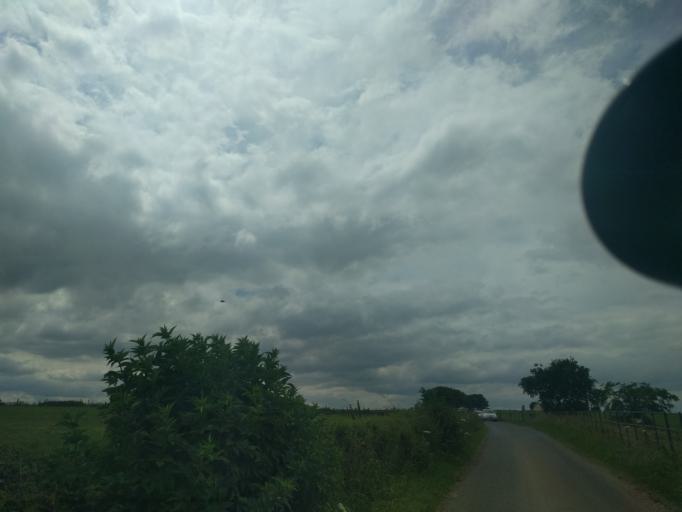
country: GB
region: England
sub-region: South Gloucestershire
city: Cold Ashton
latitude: 51.4637
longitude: -2.3559
